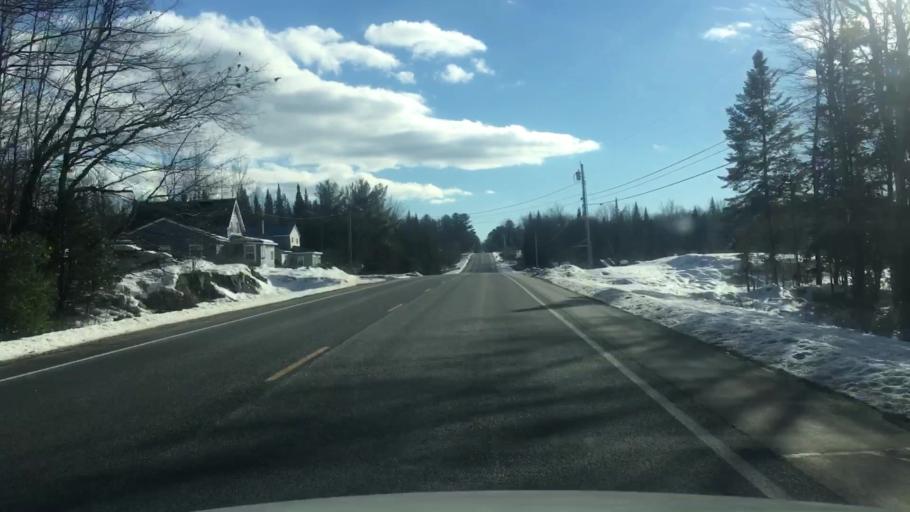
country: US
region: Maine
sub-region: Somerset County
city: Madison
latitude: 44.8446
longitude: -69.7892
